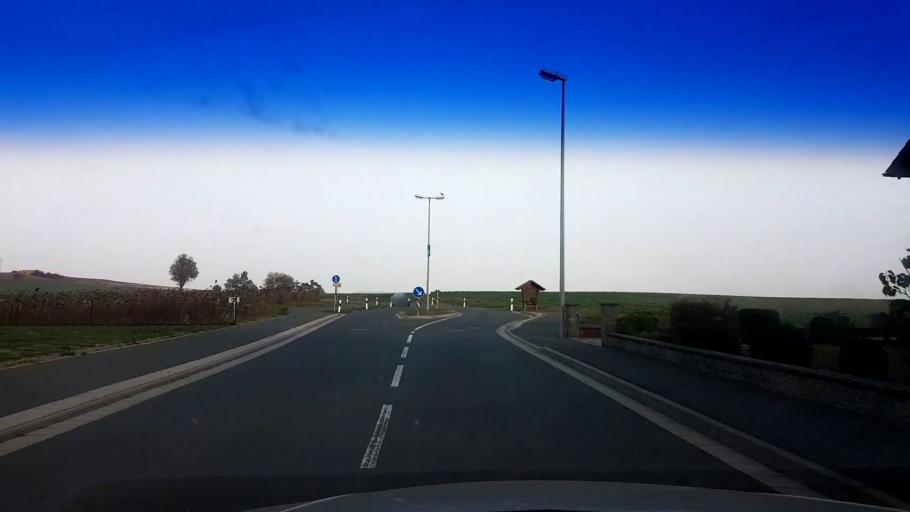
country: DE
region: Bavaria
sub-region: Upper Franconia
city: Altenkunstadt
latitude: 50.1114
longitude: 11.2540
